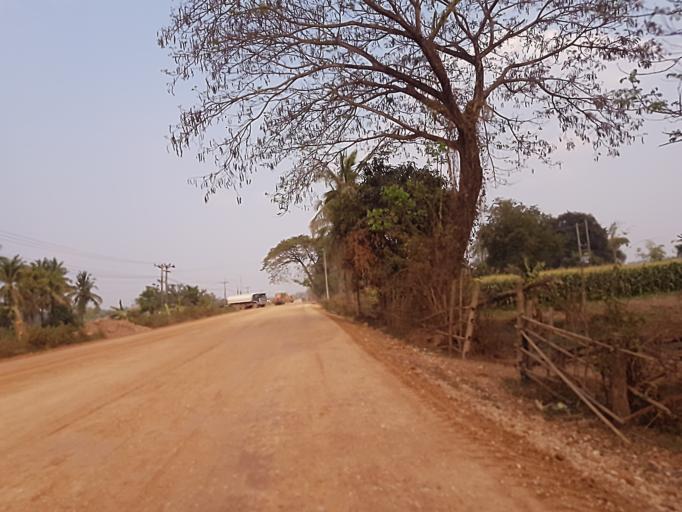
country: TH
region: Nong Khai
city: Nong Khai
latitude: 17.9800
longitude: 102.8768
